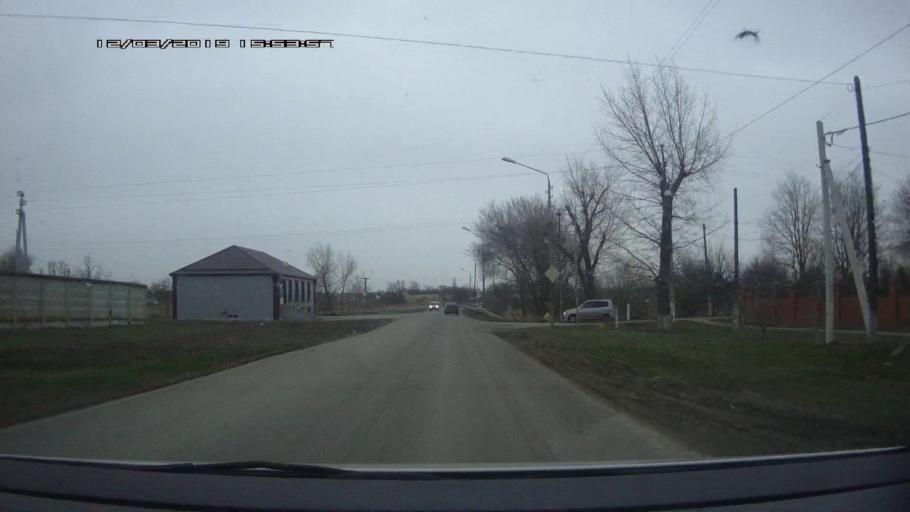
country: RU
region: Rostov
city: Novobataysk
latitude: 46.8878
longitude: 39.7768
